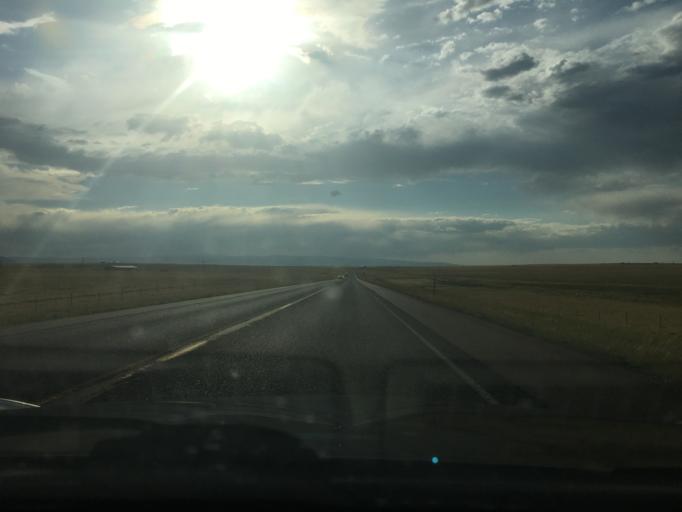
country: US
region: Wyoming
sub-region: Albany County
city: Laramie
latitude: 41.3256
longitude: -105.6732
